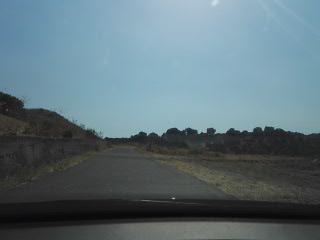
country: IT
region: Calabria
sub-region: Provincia di Reggio Calabria
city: Stignano
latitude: 38.4333
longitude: 16.4609
